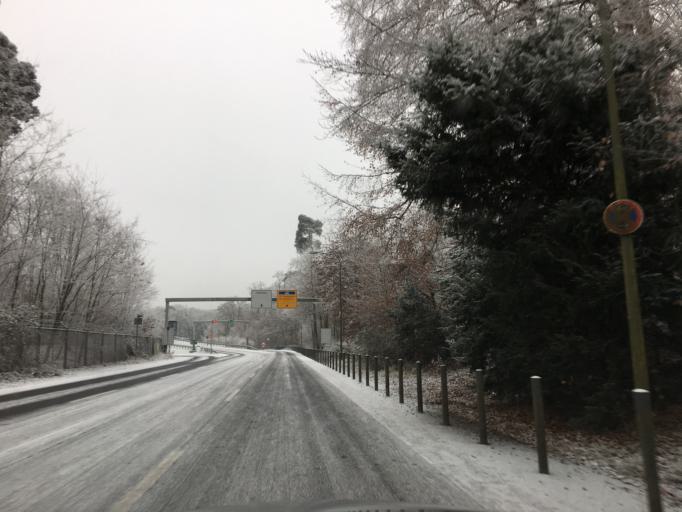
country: DE
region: Hesse
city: Niederrad
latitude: 50.0662
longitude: 8.6472
